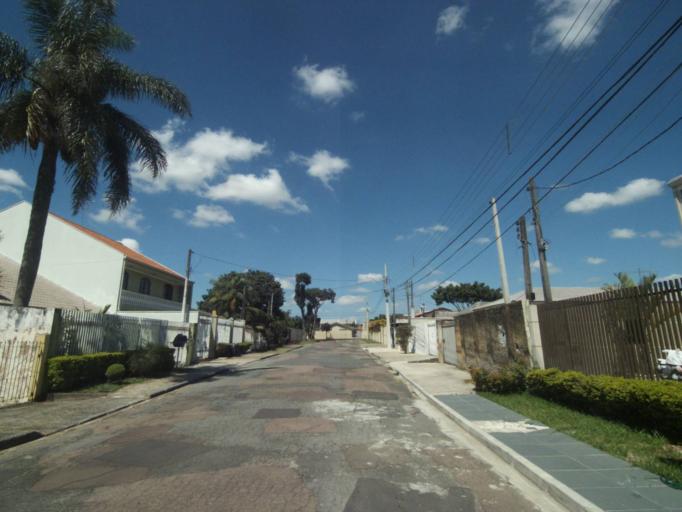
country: BR
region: Parana
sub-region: Pinhais
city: Pinhais
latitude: -25.4404
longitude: -49.2159
